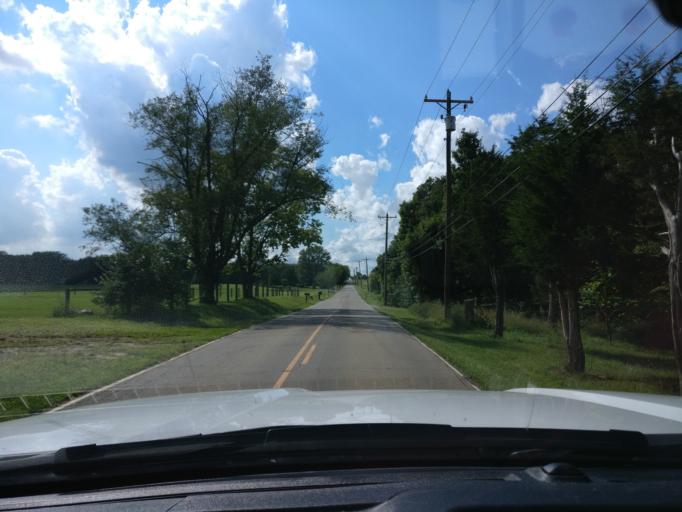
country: US
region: Ohio
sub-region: Warren County
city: Springboro
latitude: 39.5065
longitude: -84.2299
